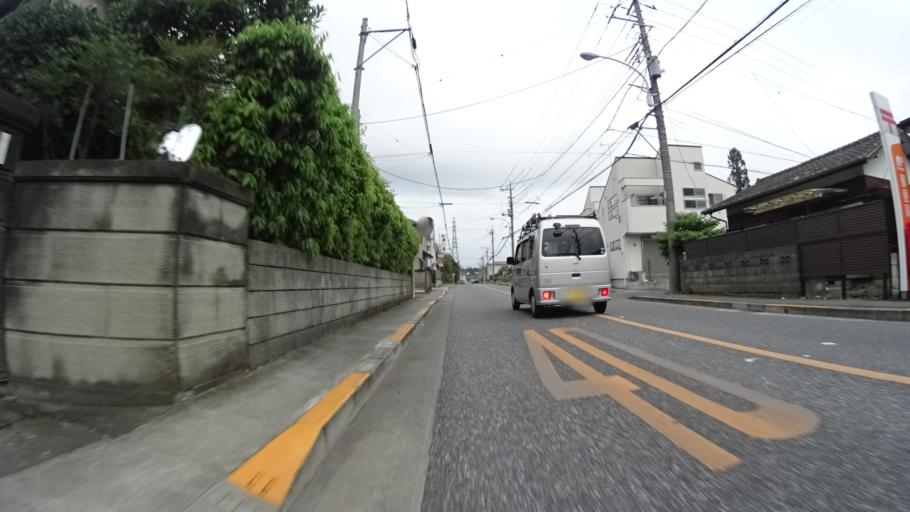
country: JP
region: Tokyo
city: Fussa
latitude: 35.7676
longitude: 139.2997
